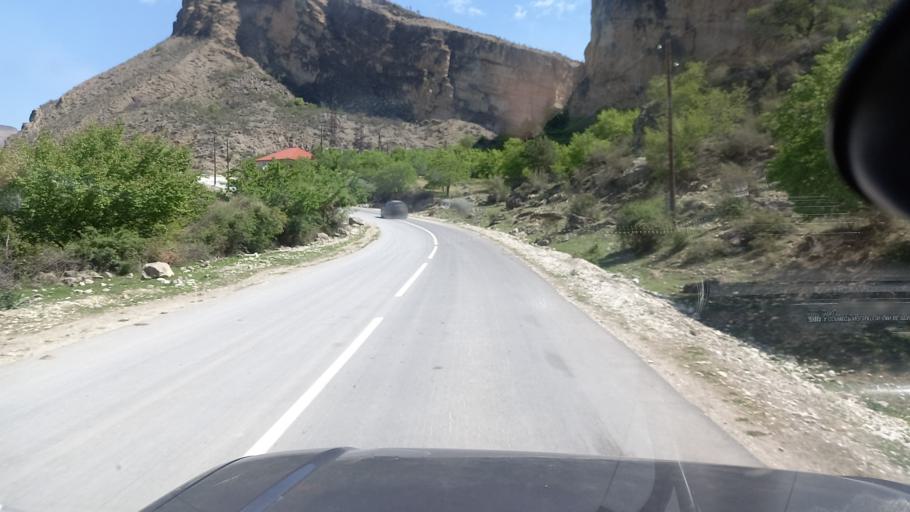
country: RU
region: Dagestan
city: Gunib
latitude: 42.4715
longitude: 46.8765
